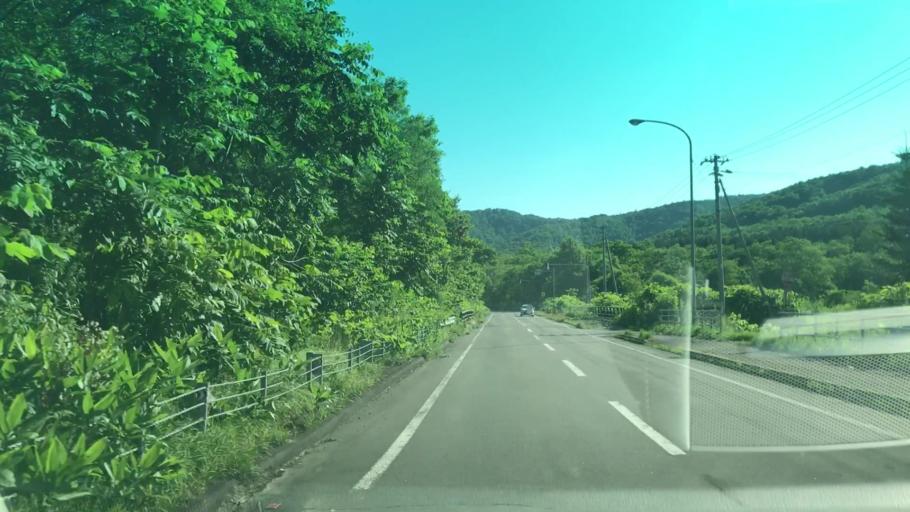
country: JP
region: Hokkaido
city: Yoichi
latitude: 43.0693
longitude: 140.7071
